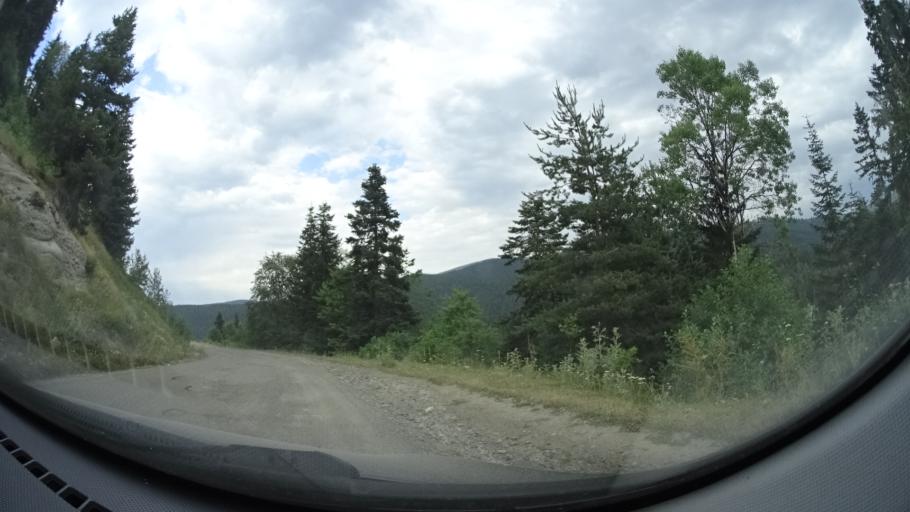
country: GE
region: Samtskhe-Javakheti
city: Adigeni
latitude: 41.6393
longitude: 42.5871
